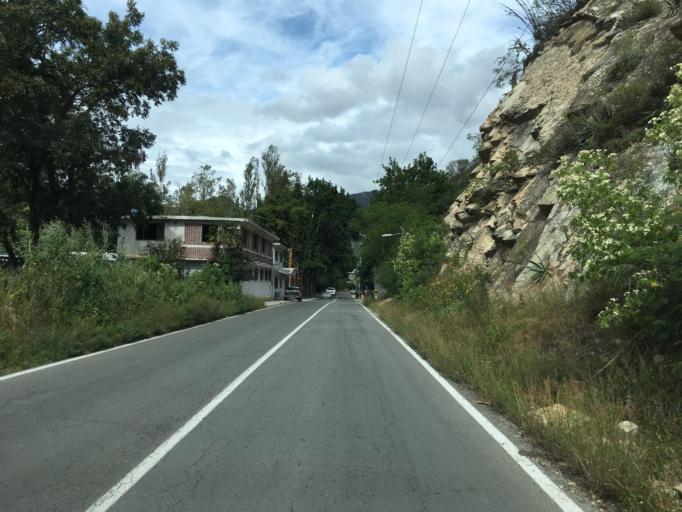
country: MX
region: Hidalgo
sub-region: San Agustin Metzquititlan
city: Mezquititlan
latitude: 20.5256
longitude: -98.7239
